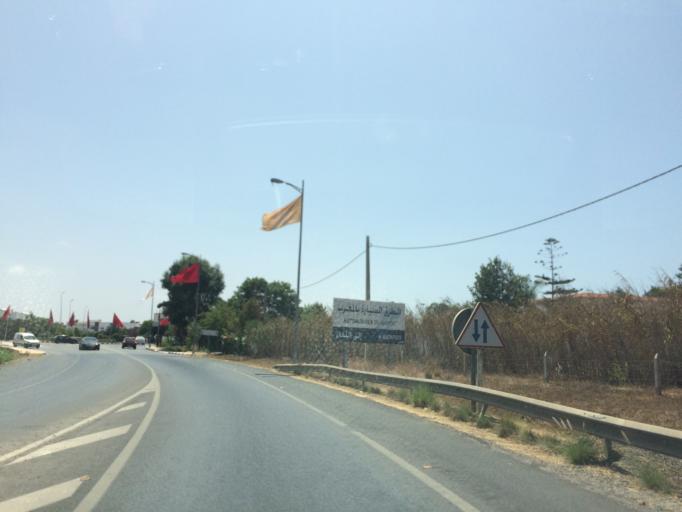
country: MA
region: Rabat-Sale-Zemmour-Zaer
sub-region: Skhirate-Temara
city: Temara
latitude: 33.9344
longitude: -6.9379
